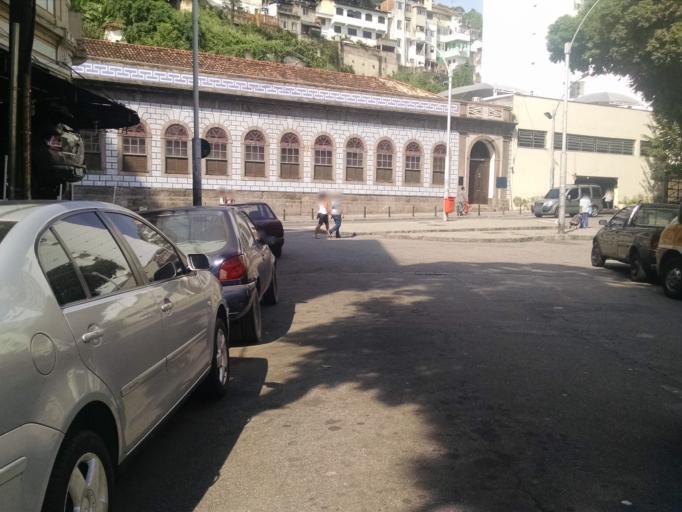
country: BR
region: Rio de Janeiro
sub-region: Rio De Janeiro
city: Rio de Janeiro
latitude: -22.9137
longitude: -43.1900
